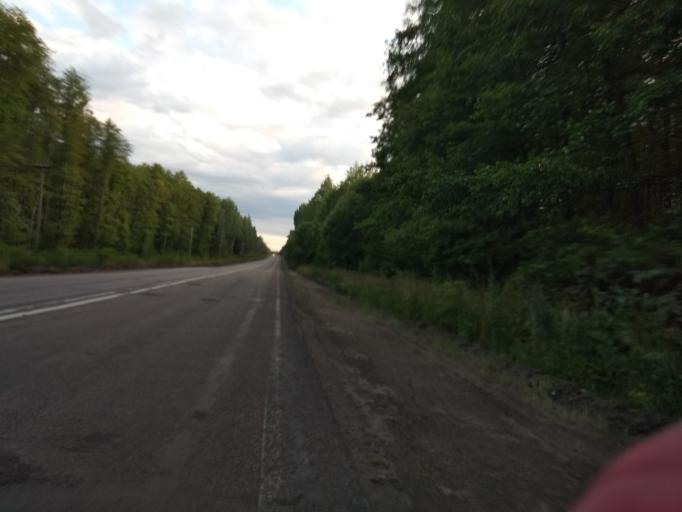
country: RU
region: Moskovskaya
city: Misheronskiy
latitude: 55.6427
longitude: 39.7555
